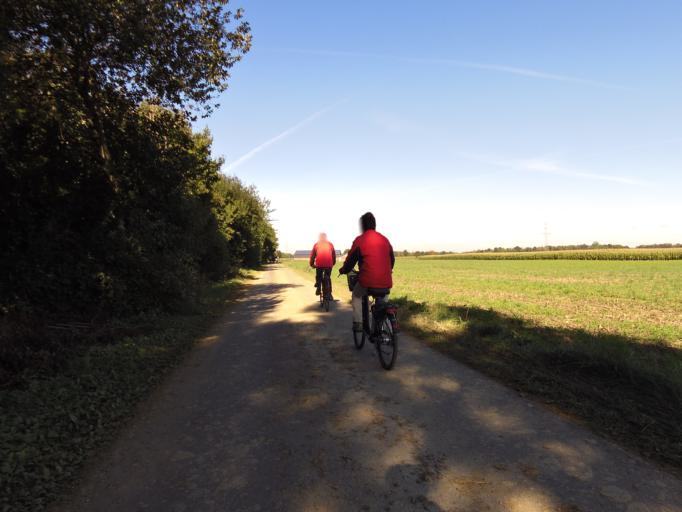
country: DE
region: North Rhine-Westphalia
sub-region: Regierungsbezirk Koln
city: Rheinbach
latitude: 50.6377
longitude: 6.9375
